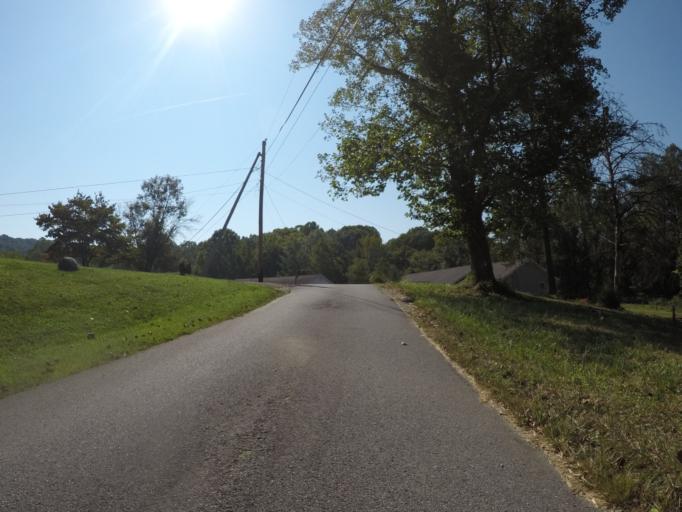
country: US
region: West Virginia
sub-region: Cabell County
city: Barboursville
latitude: 38.3771
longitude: -82.2808
